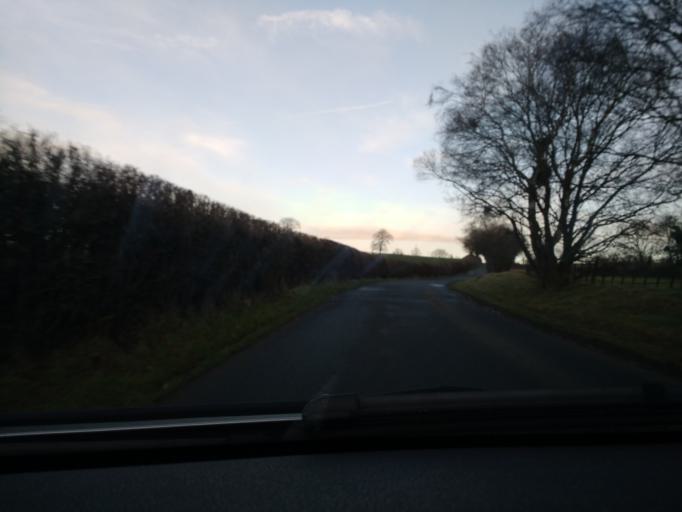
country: GB
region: England
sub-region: Cumbria
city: Carlisle
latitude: 54.7297
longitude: -2.9753
